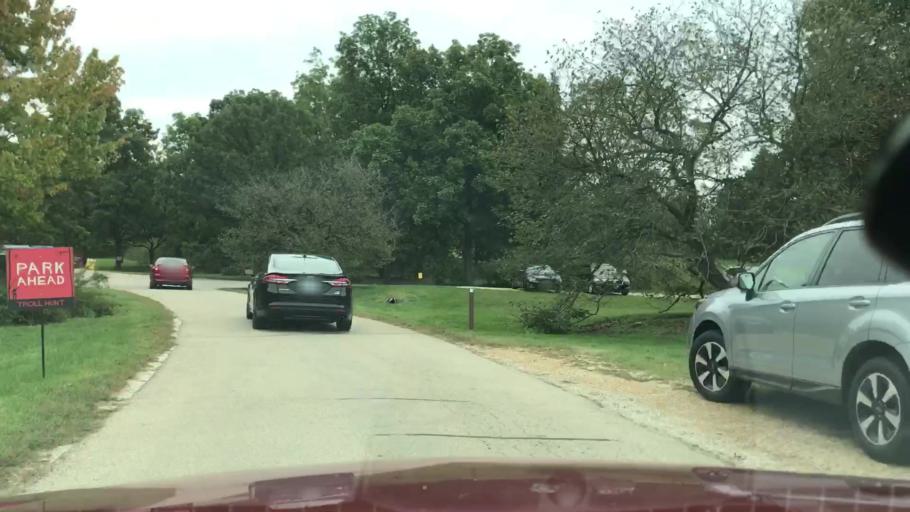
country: US
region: Illinois
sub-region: DuPage County
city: Lisle
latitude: 41.8149
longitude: -88.0674
